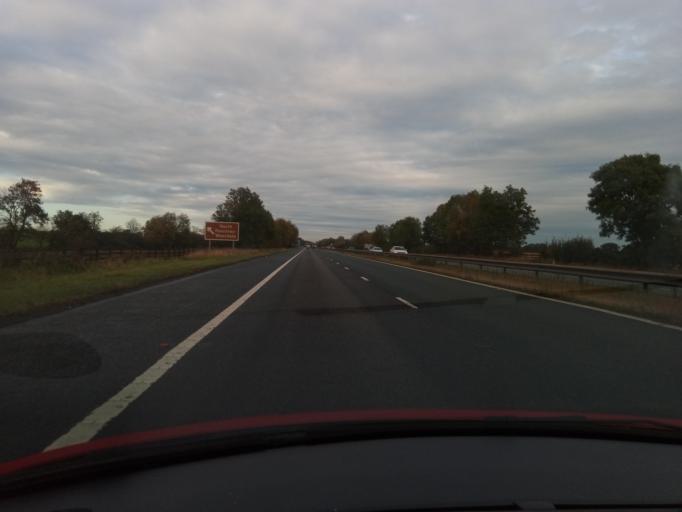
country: GB
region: England
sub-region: Darlington
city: High Coniscliffe
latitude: 54.5481
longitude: -1.6019
